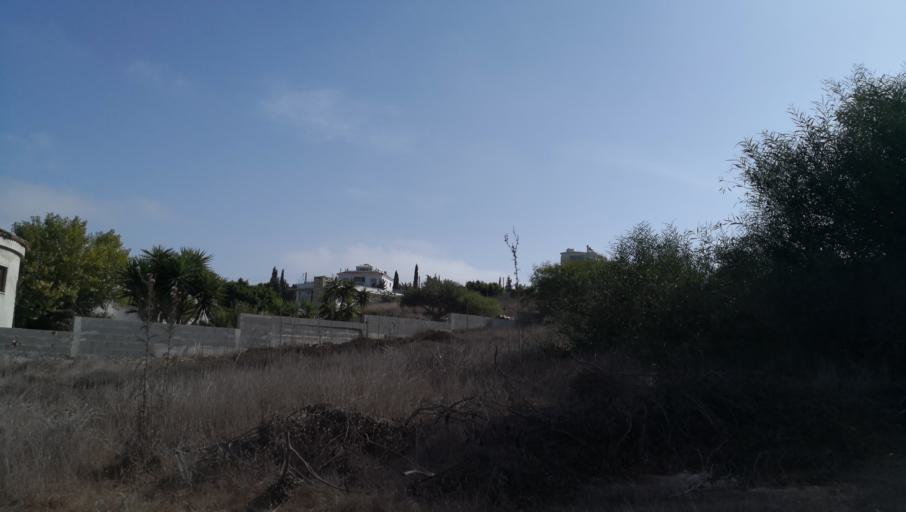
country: CY
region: Ammochostos
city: Protaras
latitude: 35.0065
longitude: 34.0265
